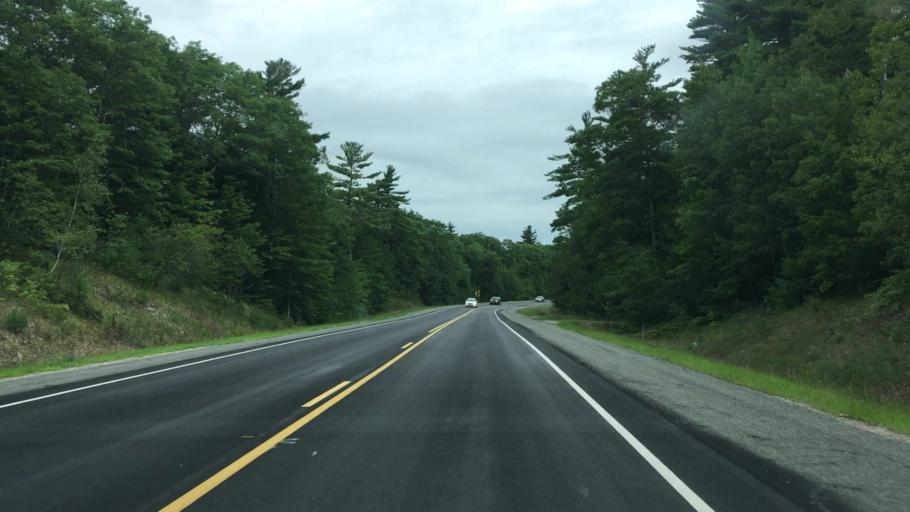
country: US
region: Maine
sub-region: Washington County
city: Cherryfield
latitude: 44.9056
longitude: -67.8568
